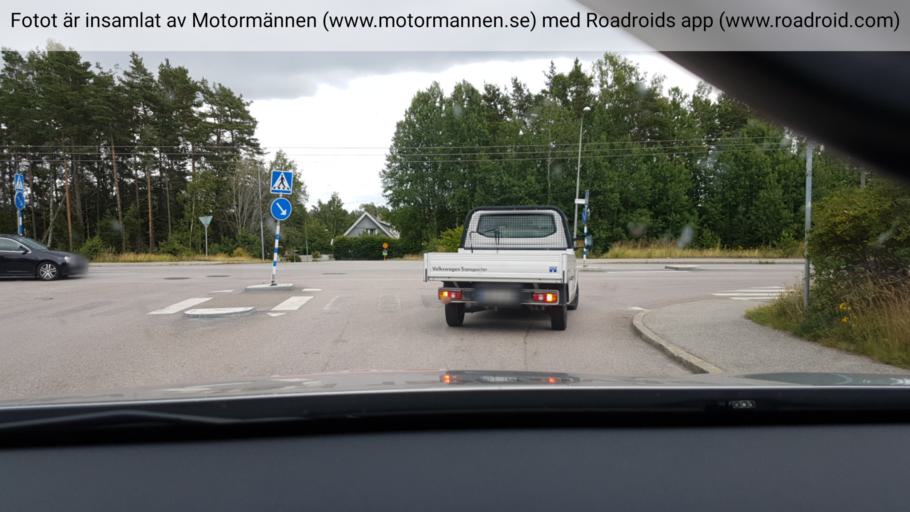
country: SE
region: Stockholm
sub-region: Nacka Kommun
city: Alta
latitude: 59.2371
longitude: 18.1940
